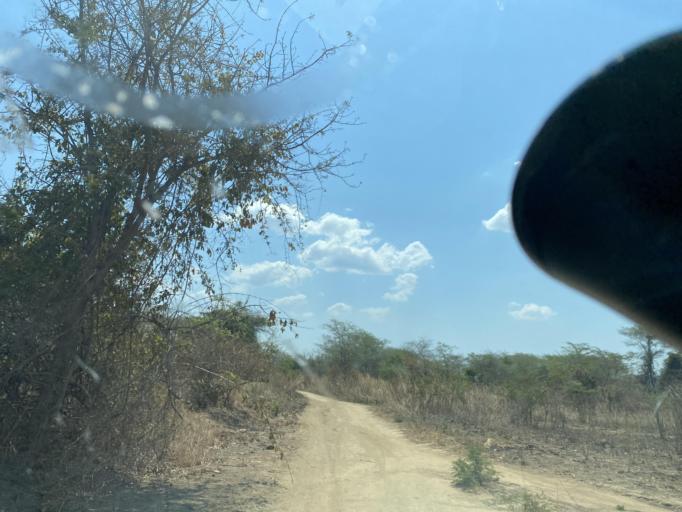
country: ZM
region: Lusaka
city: Chongwe
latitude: -15.0808
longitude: 29.5128
